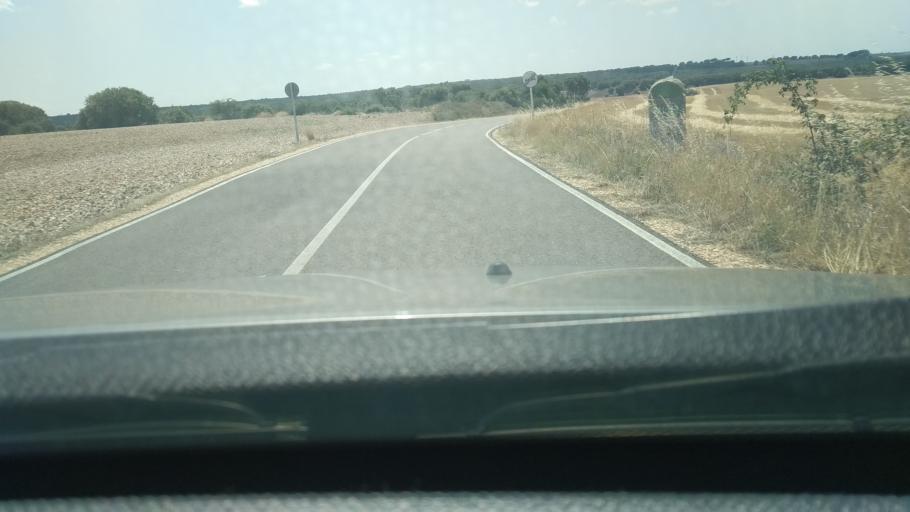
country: ES
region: Castille and Leon
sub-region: Provincia de Burgos
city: Avellanosa de Muno
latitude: 41.9737
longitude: -3.8093
